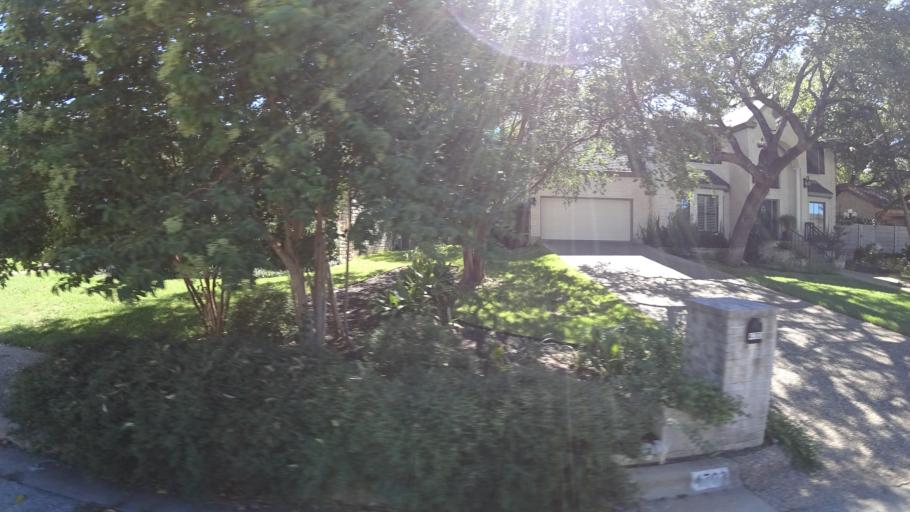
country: US
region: Texas
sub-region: Travis County
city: West Lake Hills
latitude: 30.3392
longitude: -97.7806
